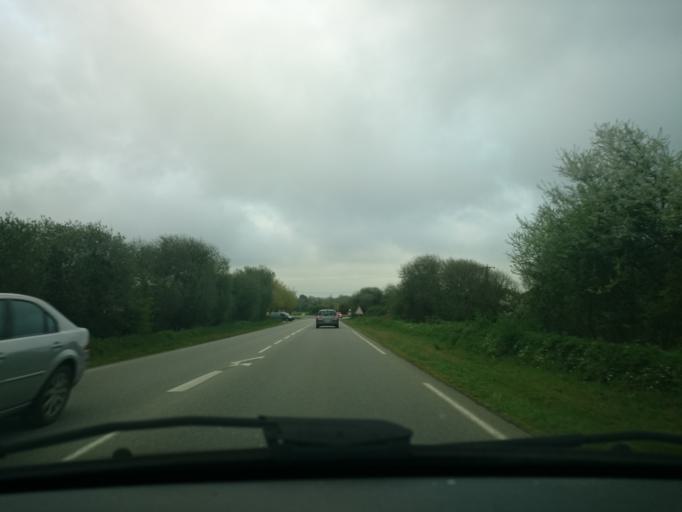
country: FR
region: Brittany
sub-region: Departement du Finistere
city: Saint-Renan
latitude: 48.4298
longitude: -4.6016
